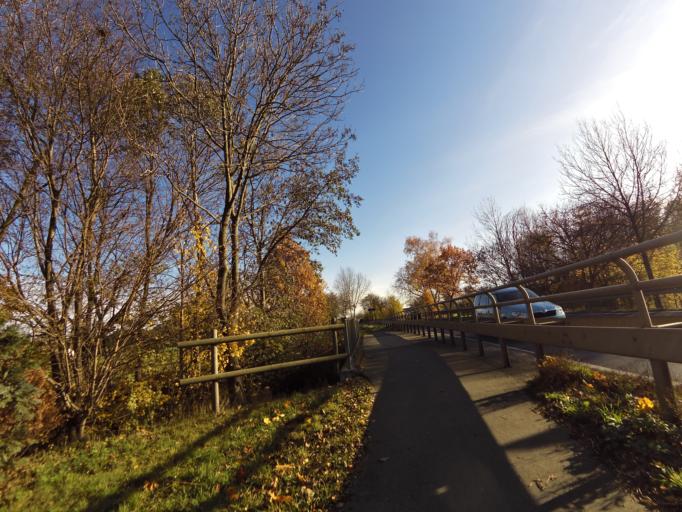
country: DE
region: North Rhine-Westphalia
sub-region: Regierungsbezirk Koln
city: Euskirchen
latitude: 50.6457
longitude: 6.8214
